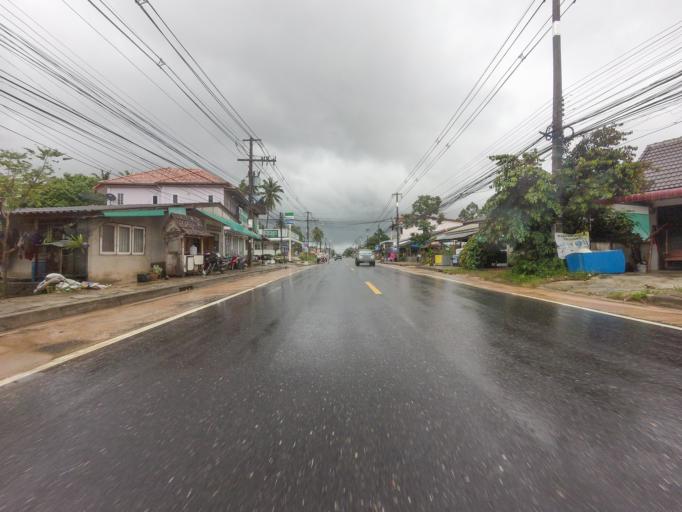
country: TH
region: Surat Thani
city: Ko Samui
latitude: 9.4527
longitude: 99.9979
